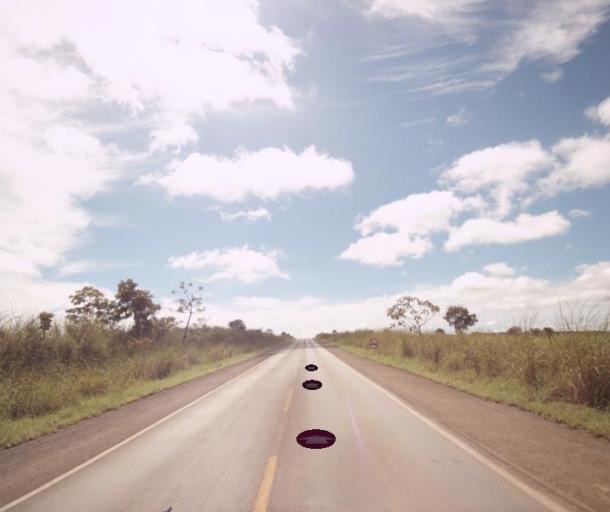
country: BR
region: Goias
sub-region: Padre Bernardo
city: Padre Bernardo
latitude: -15.2189
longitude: -48.5171
